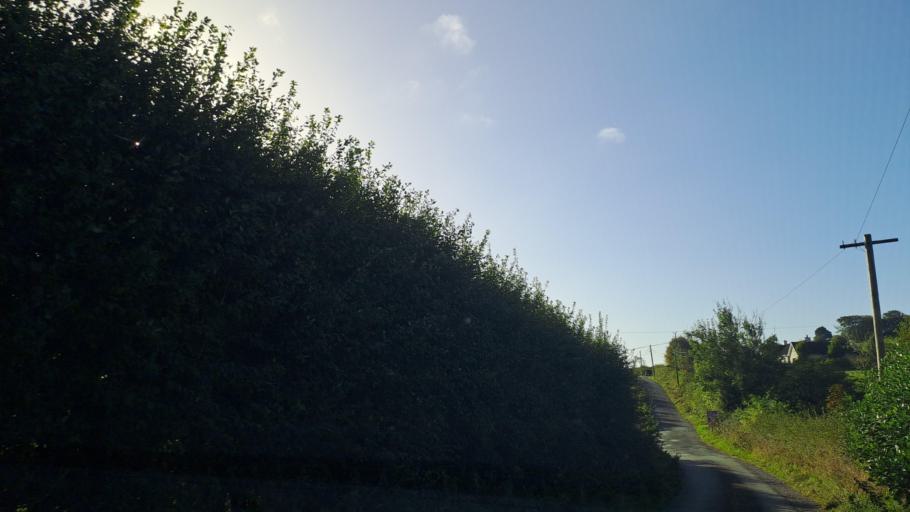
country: IE
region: Ulster
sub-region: An Cabhan
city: Kingscourt
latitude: 53.9482
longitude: -6.8770
